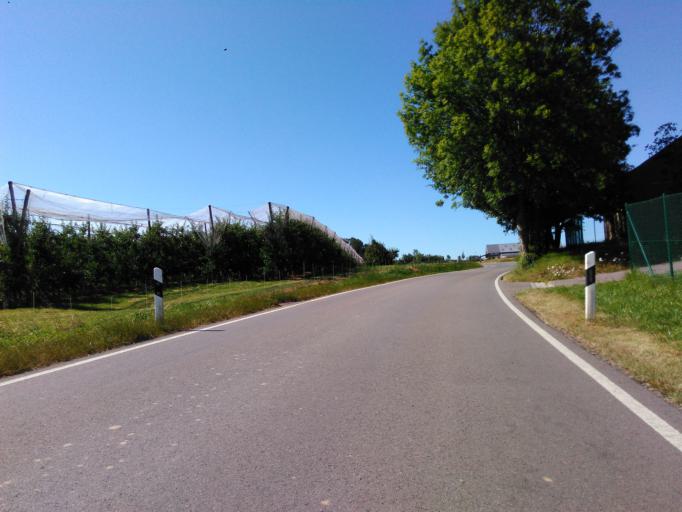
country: LU
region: Luxembourg
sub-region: Canton de Capellen
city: Dippach
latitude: 49.5625
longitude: 5.9760
